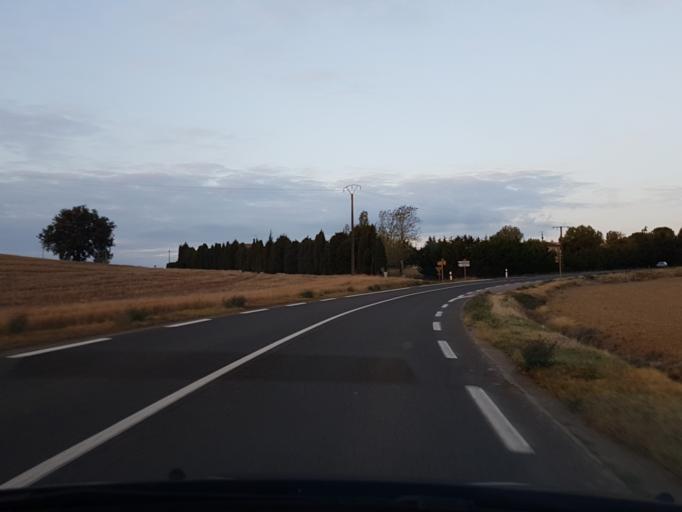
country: FR
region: Midi-Pyrenees
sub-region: Departement de l'Ariege
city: Mirepoix
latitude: 43.1463
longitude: 1.9558
